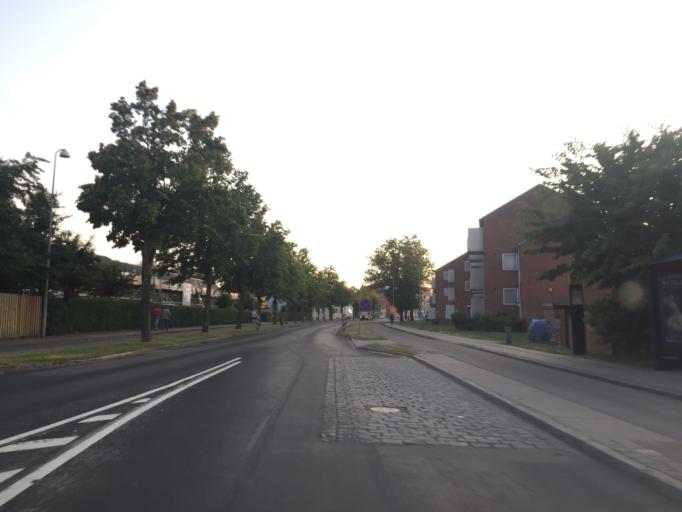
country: DK
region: Capital Region
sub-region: Hoje-Taastrup Kommune
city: Taastrup
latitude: 55.6515
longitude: 12.3075
